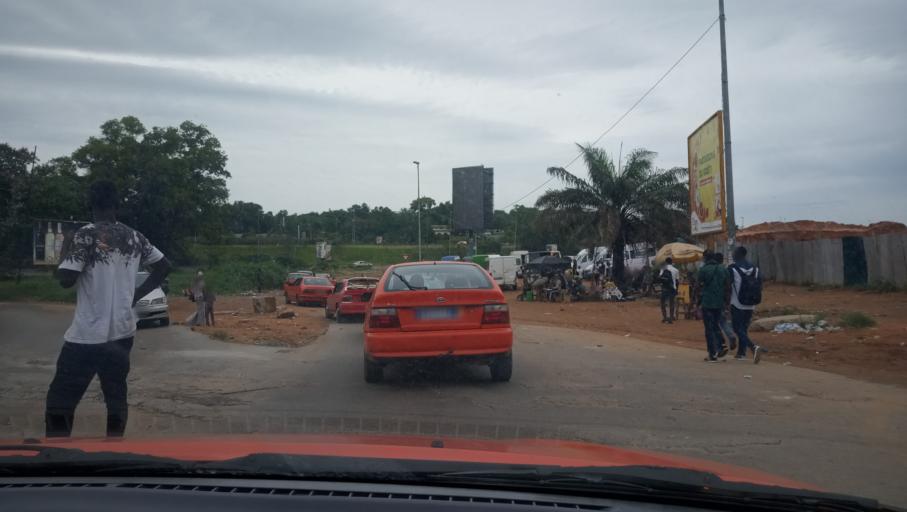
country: CI
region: Lagunes
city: Abidjan
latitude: 5.3530
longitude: -4.0120
